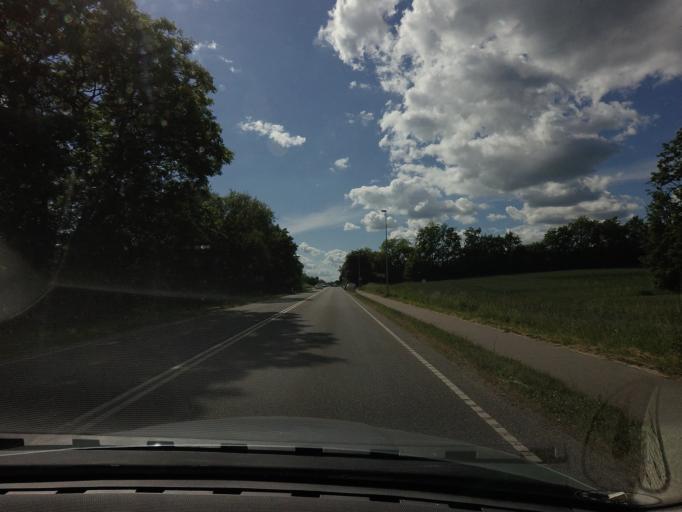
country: DK
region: Central Jutland
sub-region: Syddjurs Kommune
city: Ronde
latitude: 56.3055
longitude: 10.4454
